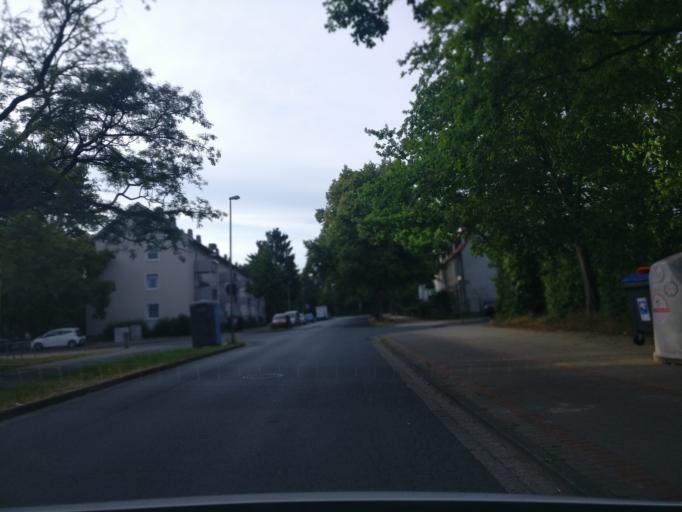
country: DE
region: Lower Saxony
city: Laatzen
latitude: 52.3341
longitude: 9.7871
